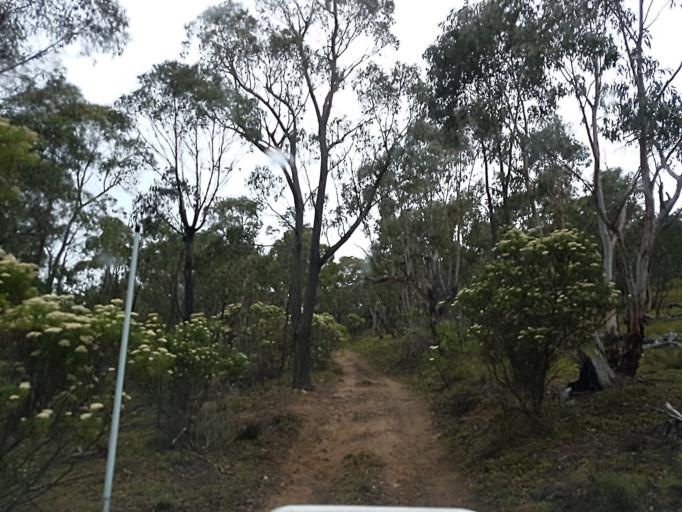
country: AU
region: New South Wales
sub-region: Snowy River
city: Jindabyne
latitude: -36.8794
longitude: 148.3388
